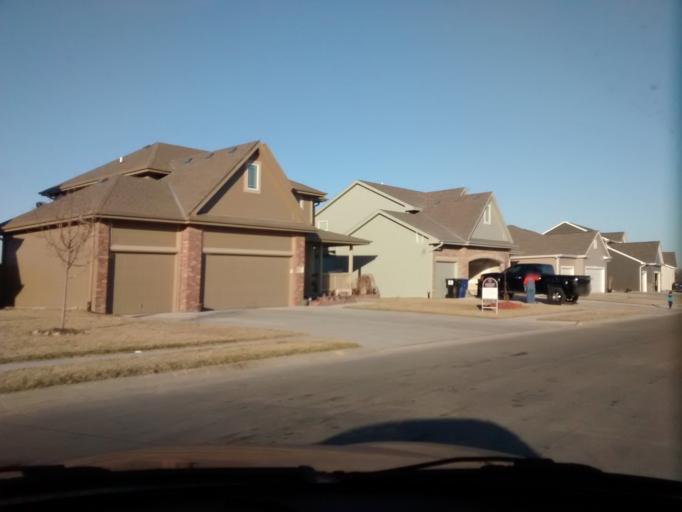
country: US
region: Nebraska
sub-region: Sarpy County
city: Papillion
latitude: 41.1451
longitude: -95.9816
